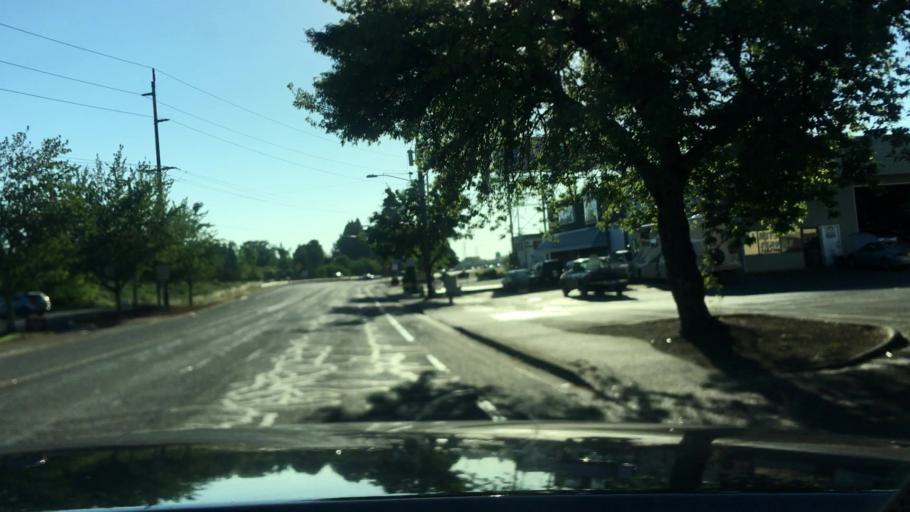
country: US
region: Oregon
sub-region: Lane County
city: Springfield
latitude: 44.0621
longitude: -123.0274
